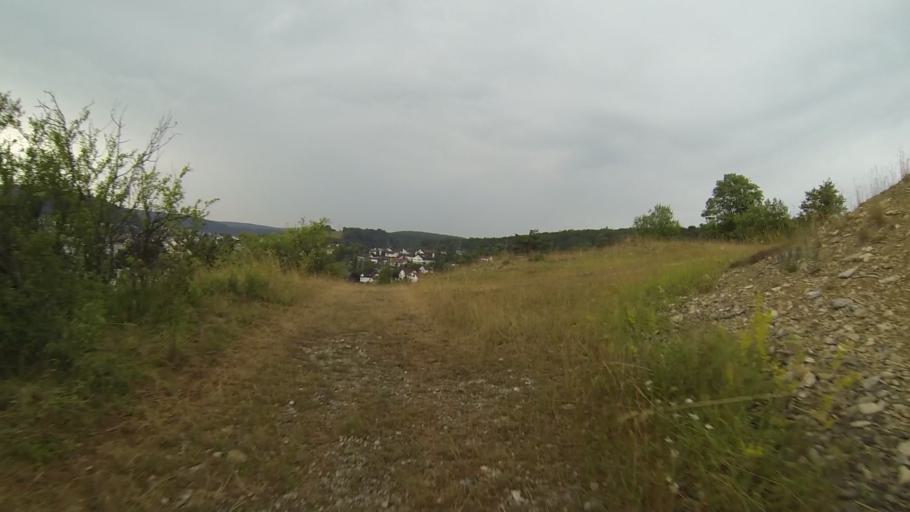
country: DE
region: Baden-Wuerttemberg
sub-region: Regierungsbezirk Stuttgart
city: Heidenheim an der Brenz
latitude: 48.7009
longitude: 10.1746
